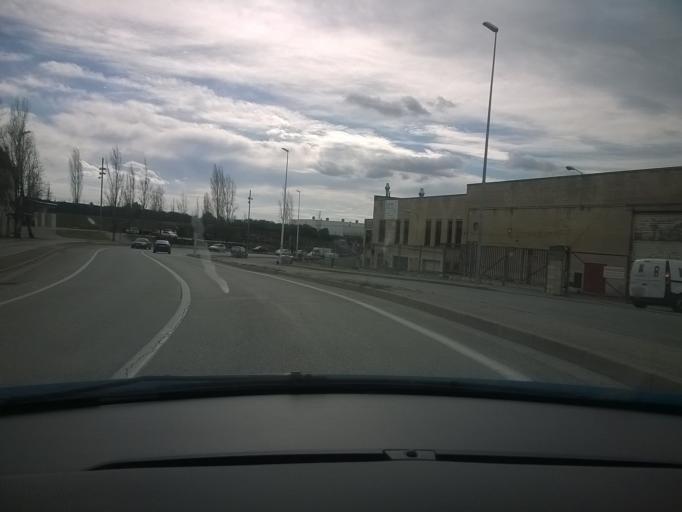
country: ES
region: Catalonia
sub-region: Provincia de Barcelona
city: Rubi
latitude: 41.5073
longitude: 2.0420
